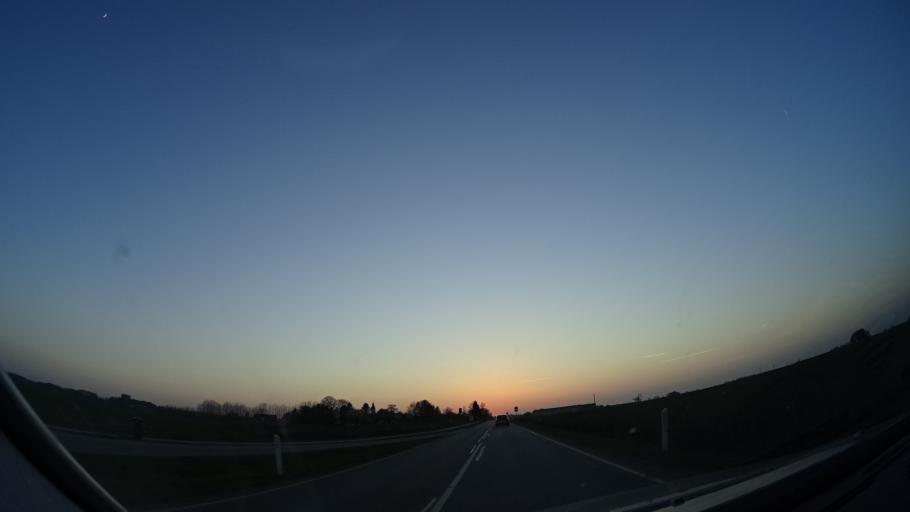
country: DK
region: Zealand
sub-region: Lejre Kommune
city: Ejby
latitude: 55.6572
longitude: 11.9162
